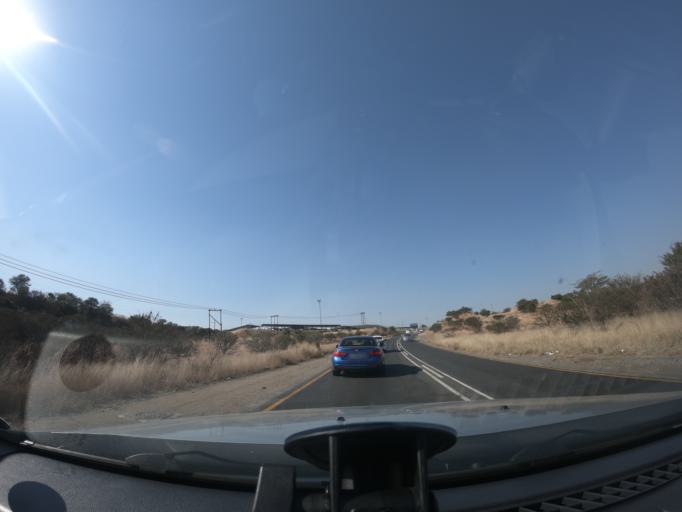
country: ZA
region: KwaZulu-Natal
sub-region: uThukela District Municipality
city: Ladysmith
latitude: -28.5482
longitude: 29.8275
